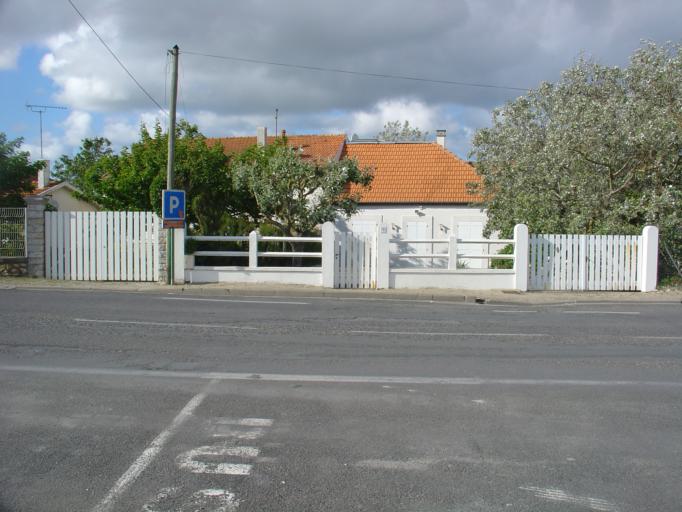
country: FR
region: Poitou-Charentes
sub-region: Departement de la Charente-Maritime
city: Dolus-d'Oleron
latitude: 45.9148
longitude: -1.3252
